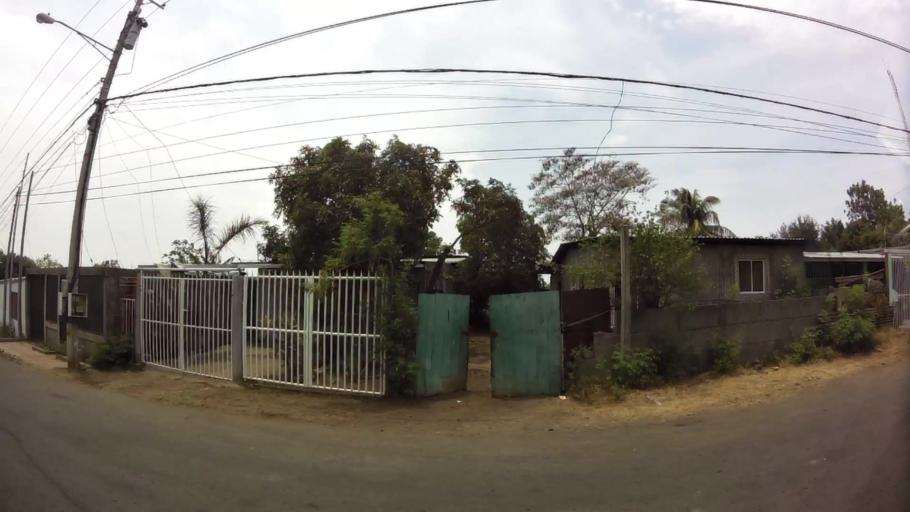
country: NI
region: Managua
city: Ciudad Sandino
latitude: 12.1329
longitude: -86.3086
